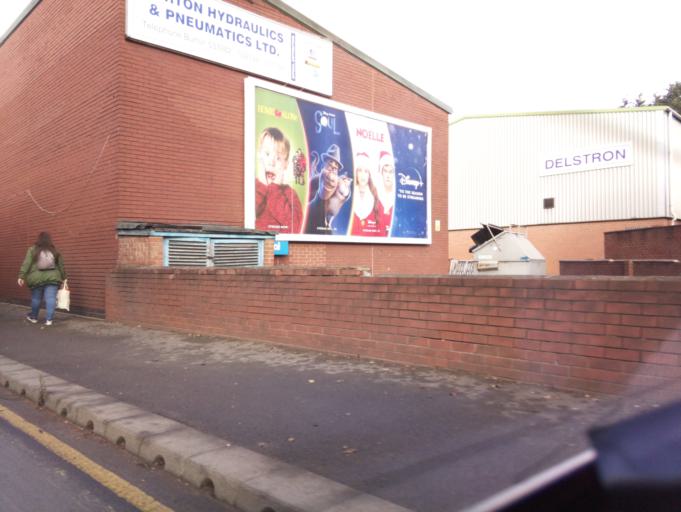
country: GB
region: England
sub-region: Staffordshire
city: Burton upon Trent
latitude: 52.7998
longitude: -1.6408
